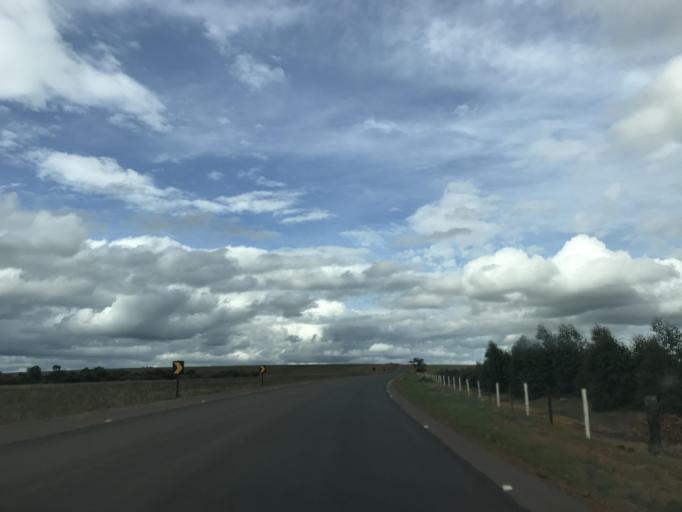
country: BR
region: Goias
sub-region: Vianopolis
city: Vianopolis
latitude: -16.9794
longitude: -48.6664
